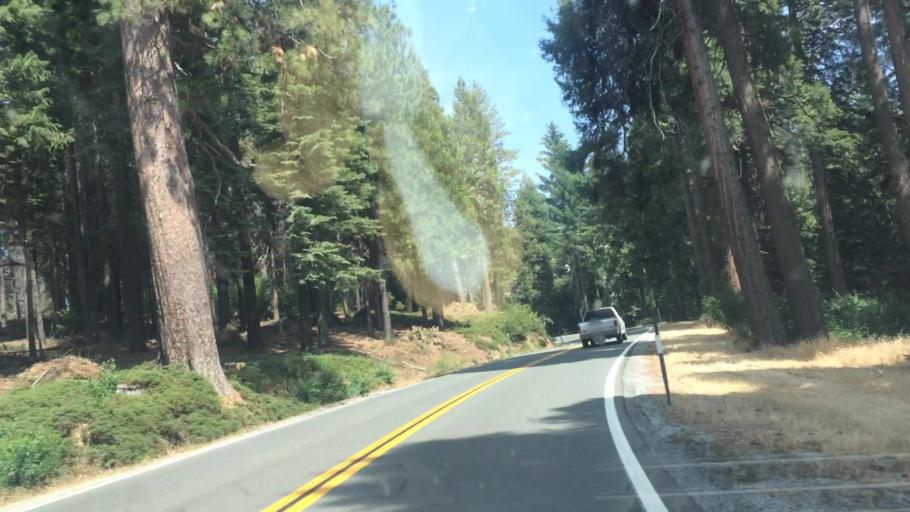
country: US
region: California
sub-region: Amador County
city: Pioneer
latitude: 38.5220
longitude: -120.4496
